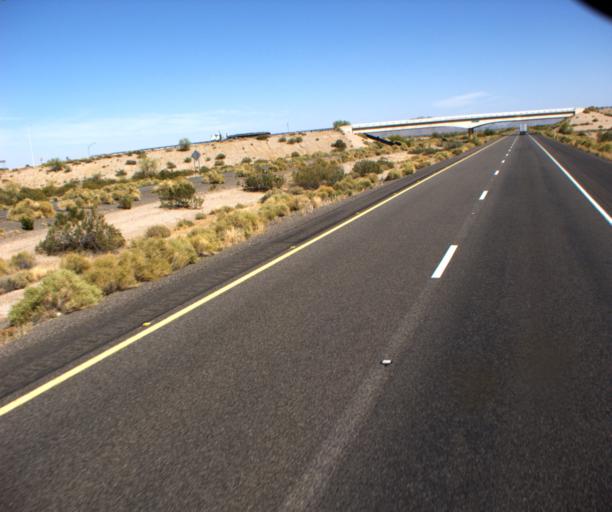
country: US
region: Arizona
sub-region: Maricopa County
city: Gila Bend
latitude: 32.9257
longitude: -112.6738
